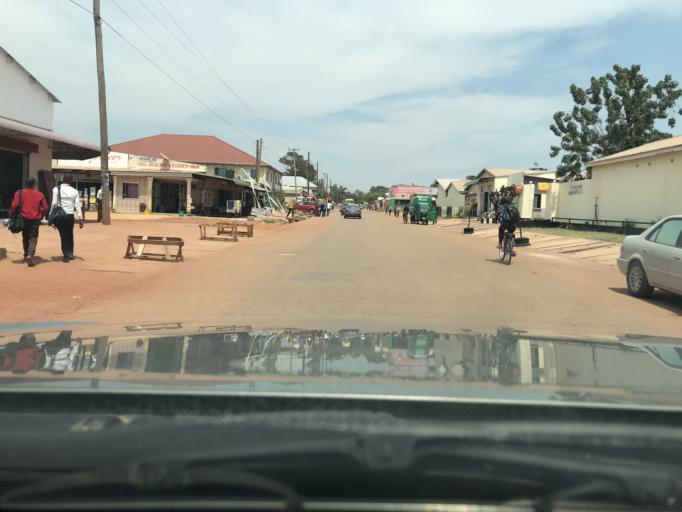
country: ZM
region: Northern
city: Kasama
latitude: -10.2048
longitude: 31.1888
